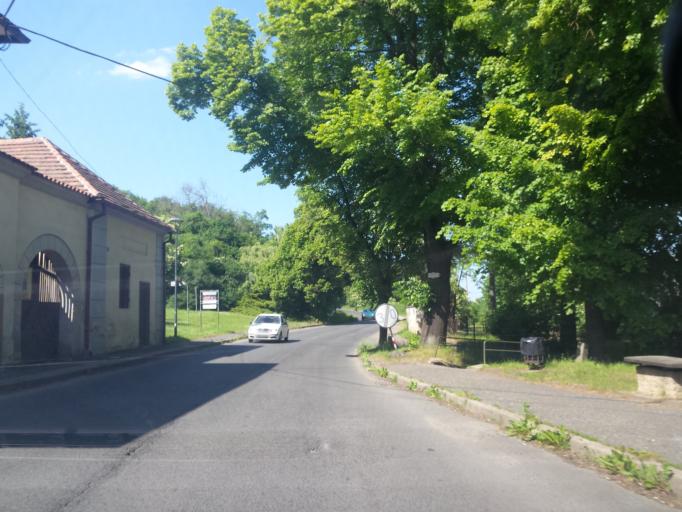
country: CZ
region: Central Bohemia
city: Nelahozeves
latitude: 50.2623
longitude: 14.3016
